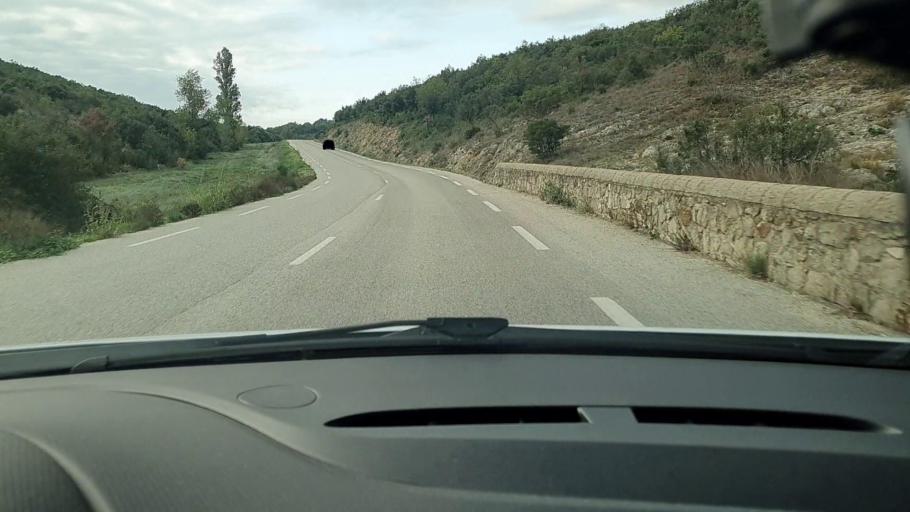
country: FR
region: Languedoc-Roussillon
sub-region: Departement du Gard
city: Mons
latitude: 44.1241
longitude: 4.2236
